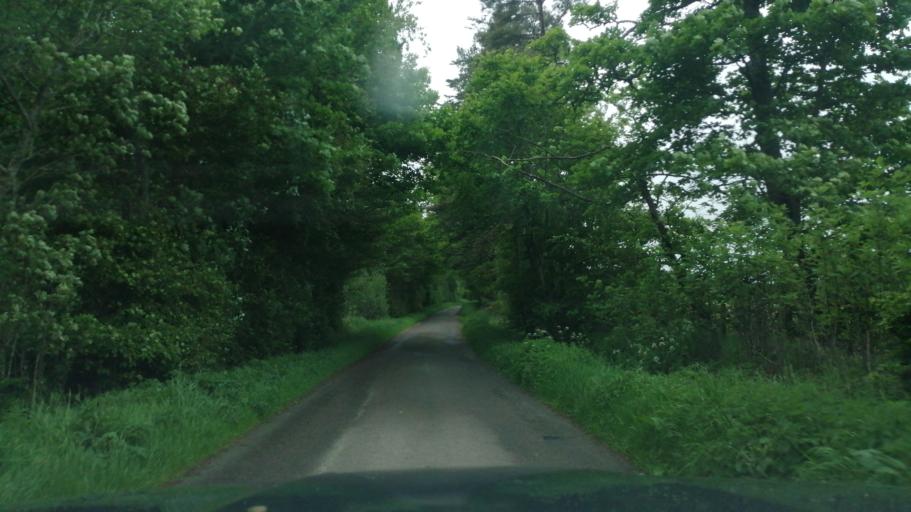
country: GB
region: Scotland
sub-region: Moray
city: Keith
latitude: 57.5666
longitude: -2.8608
